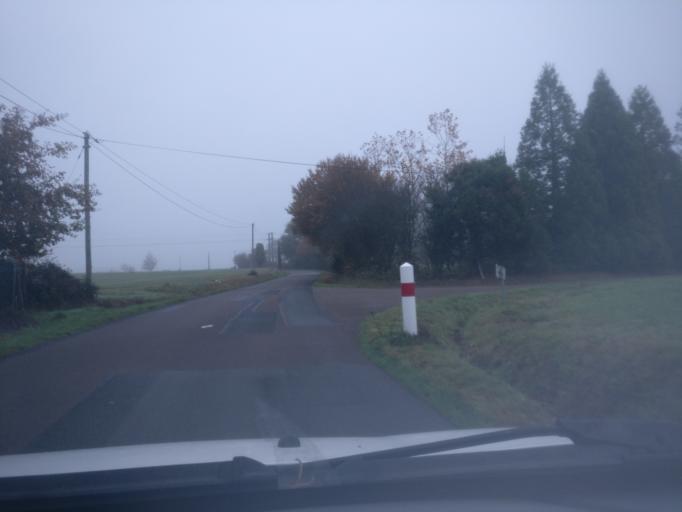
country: FR
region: Brittany
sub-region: Departement d'Ille-et-Vilaine
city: Bruz
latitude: 48.0069
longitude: -1.7700
